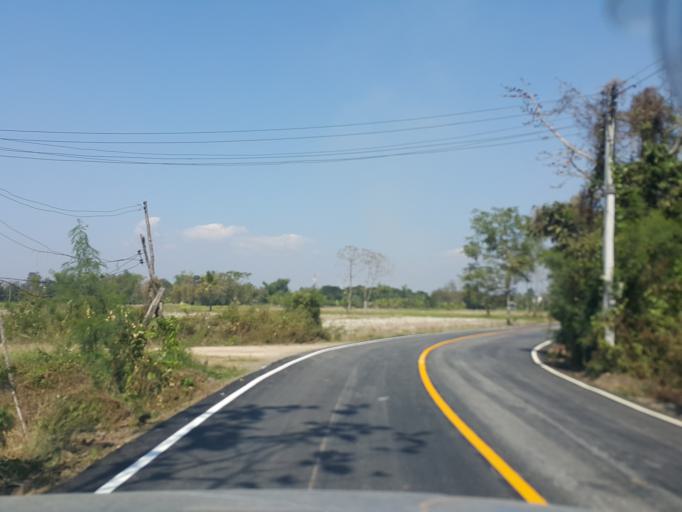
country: TH
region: Chiang Mai
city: San Kamphaeng
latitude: 18.8000
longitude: 99.1237
